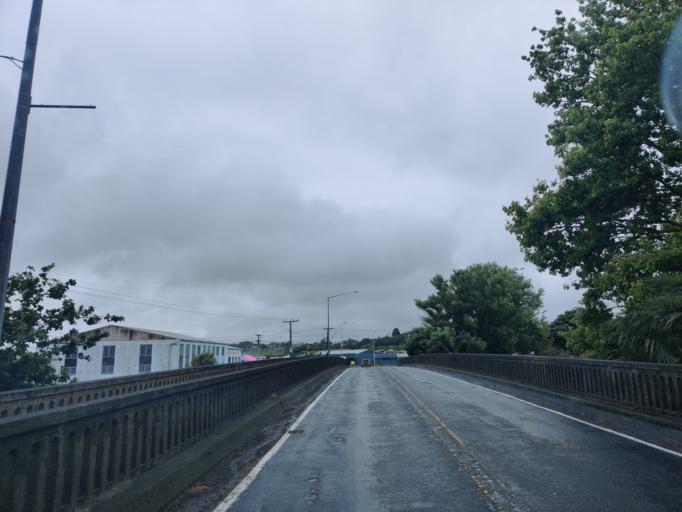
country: NZ
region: Northland
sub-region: Kaipara District
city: Dargaville
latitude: -35.9452
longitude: 173.8664
